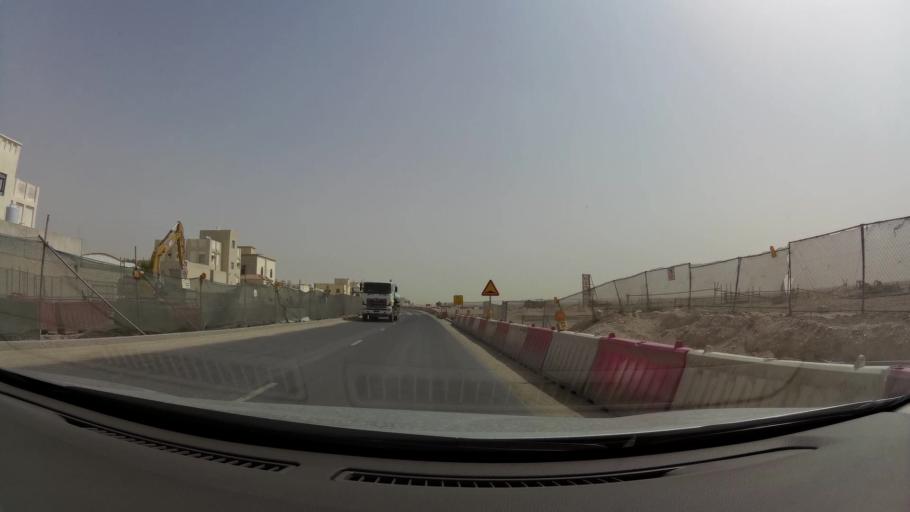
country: QA
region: Baladiyat ar Rayyan
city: Ar Rayyan
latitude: 25.2468
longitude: 51.3623
